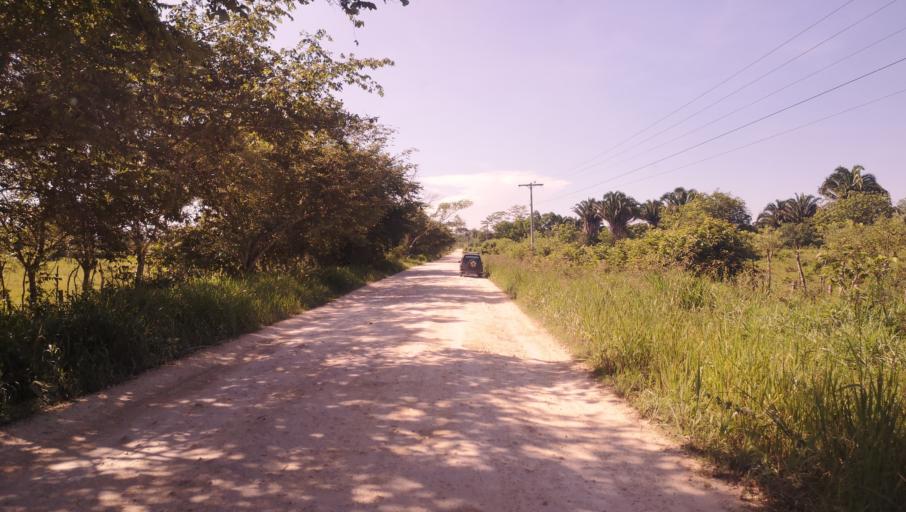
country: GT
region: Peten
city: Dolores
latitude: 16.7190
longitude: -89.3716
